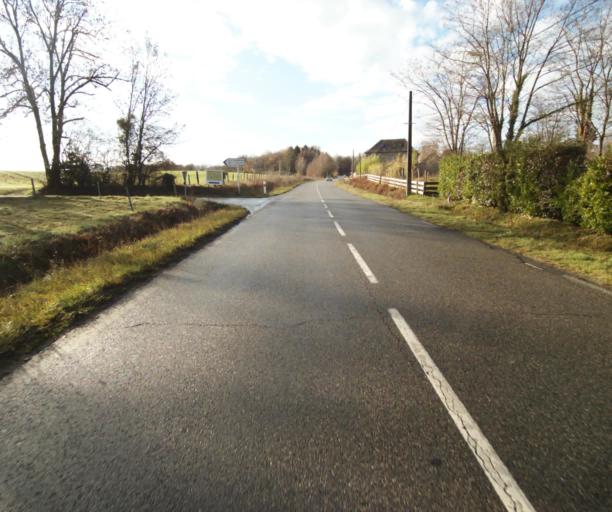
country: FR
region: Limousin
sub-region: Departement de la Correze
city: Saint-Mexant
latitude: 45.2530
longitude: 1.6318
